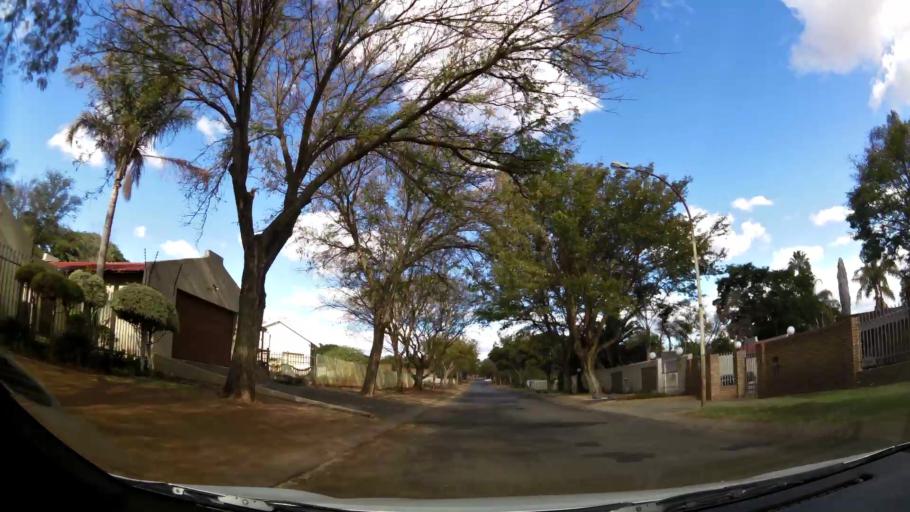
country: ZA
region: Limpopo
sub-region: Capricorn District Municipality
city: Polokwane
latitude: -23.8927
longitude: 29.4814
